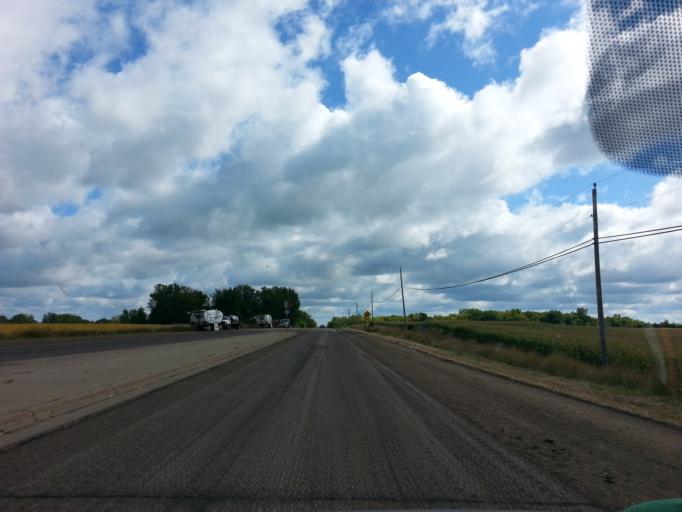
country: US
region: Minnesota
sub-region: Washington County
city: Oakdale
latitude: 44.9634
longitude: -92.9296
